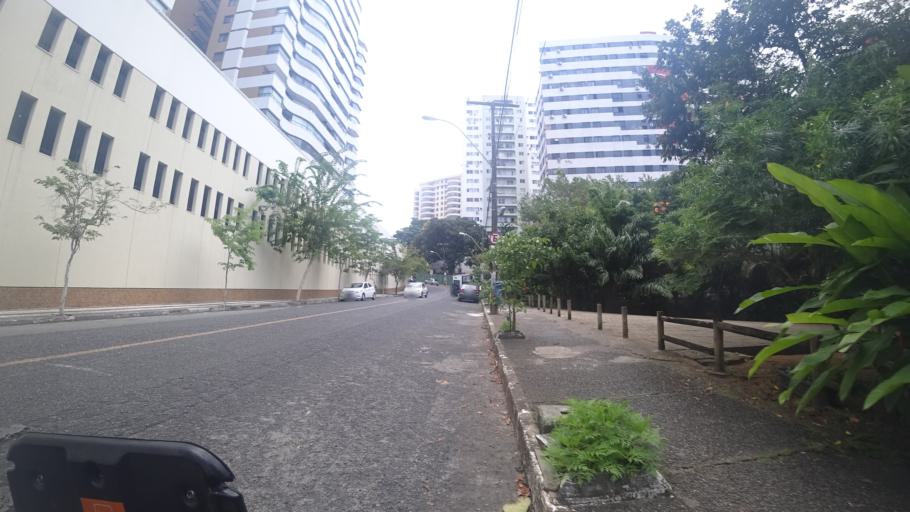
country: BR
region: Bahia
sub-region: Salvador
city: Salvador
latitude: -12.9947
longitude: -38.4723
